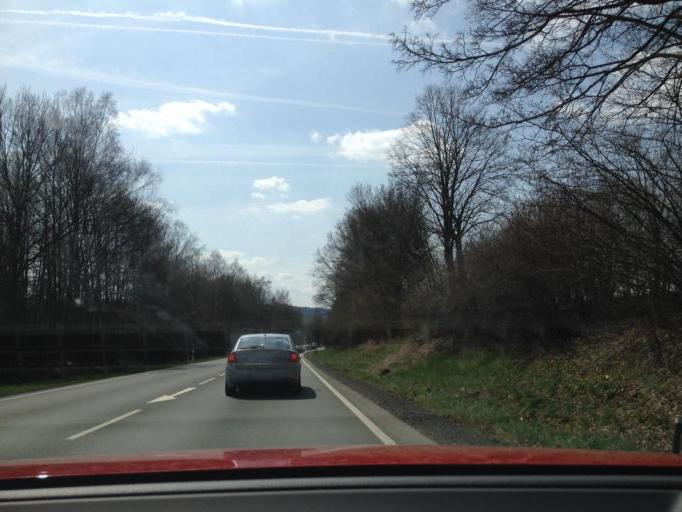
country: DE
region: Bavaria
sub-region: Upper Franconia
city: Arzberg
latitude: 50.0313
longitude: 12.1517
